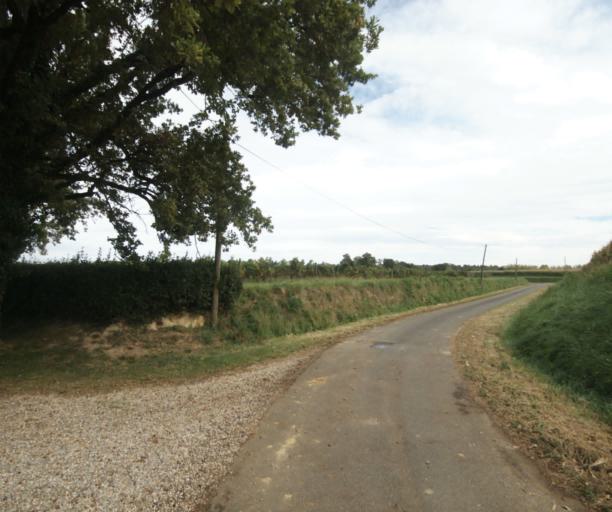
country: FR
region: Aquitaine
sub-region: Departement des Landes
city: Villeneuve-de-Marsan
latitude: 43.9071
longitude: -0.2100
